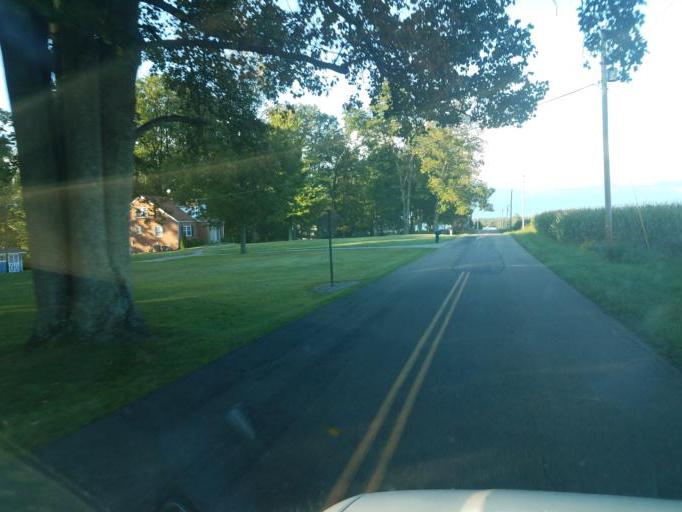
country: US
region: Ohio
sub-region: Knox County
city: Fredericktown
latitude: 40.4175
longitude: -82.5977
